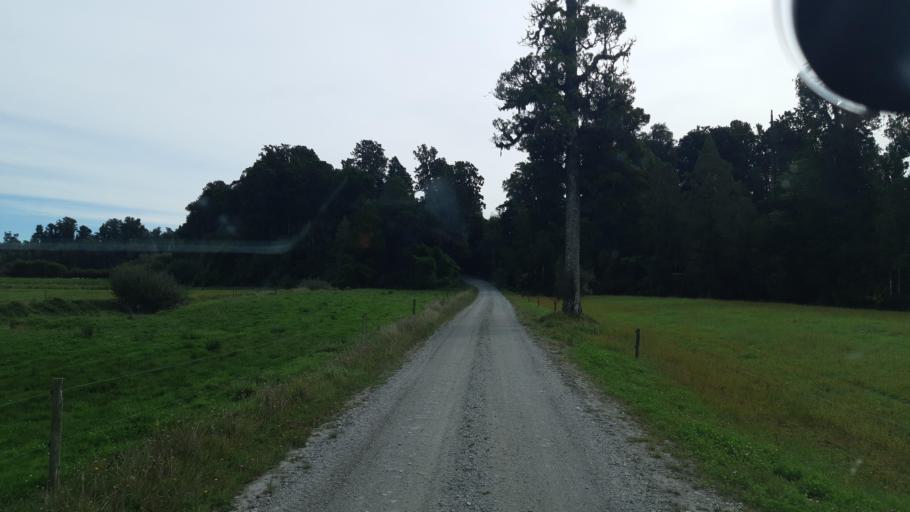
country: NZ
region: West Coast
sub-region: Westland District
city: Hokitika
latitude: -43.1116
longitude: 170.4745
